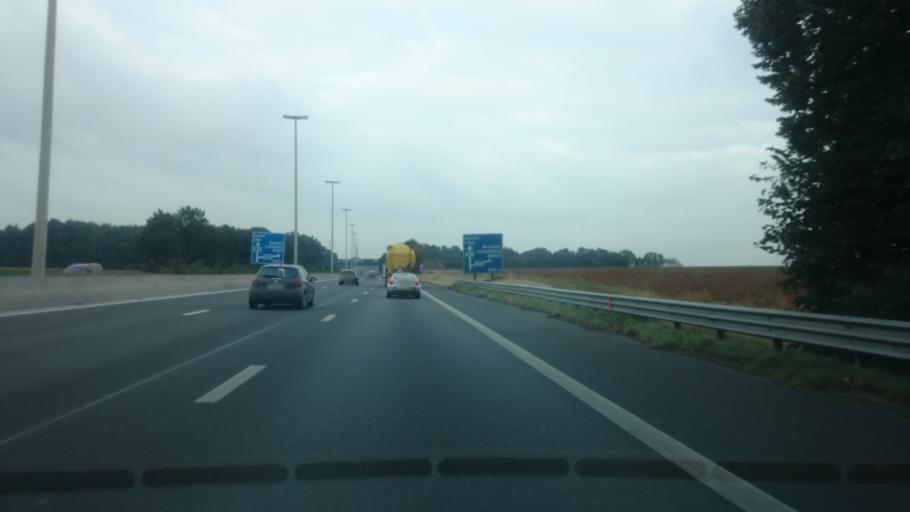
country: BE
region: Wallonia
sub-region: Province de Namur
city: Namur
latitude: 50.5117
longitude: 4.8559
